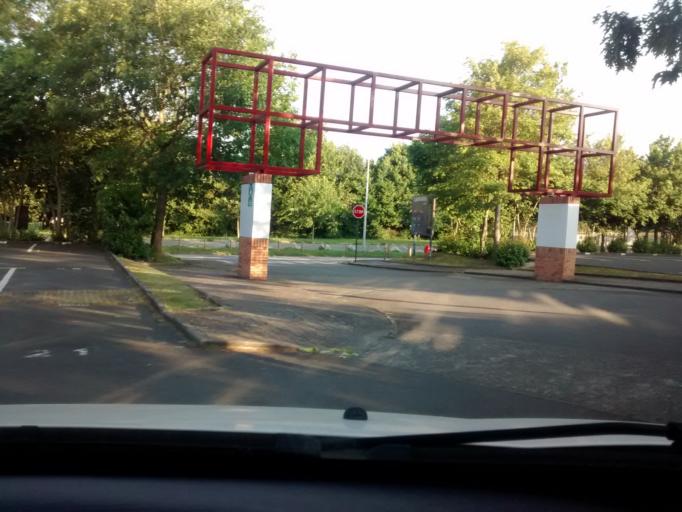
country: FR
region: Brittany
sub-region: Departement d'Ille-et-Vilaine
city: Cesson-Sevigne
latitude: 48.1320
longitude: -1.6240
